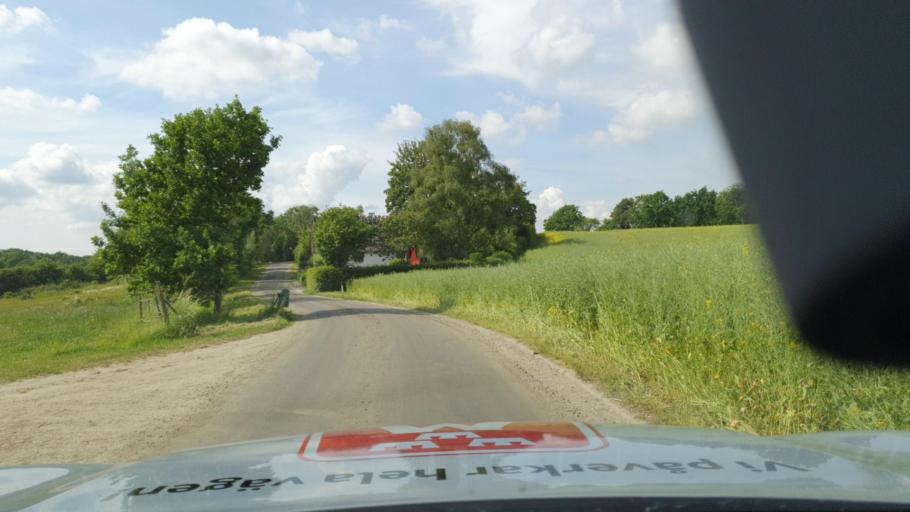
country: SE
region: Skane
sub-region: Skurups Kommun
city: Skurup
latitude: 55.5359
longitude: 13.5361
